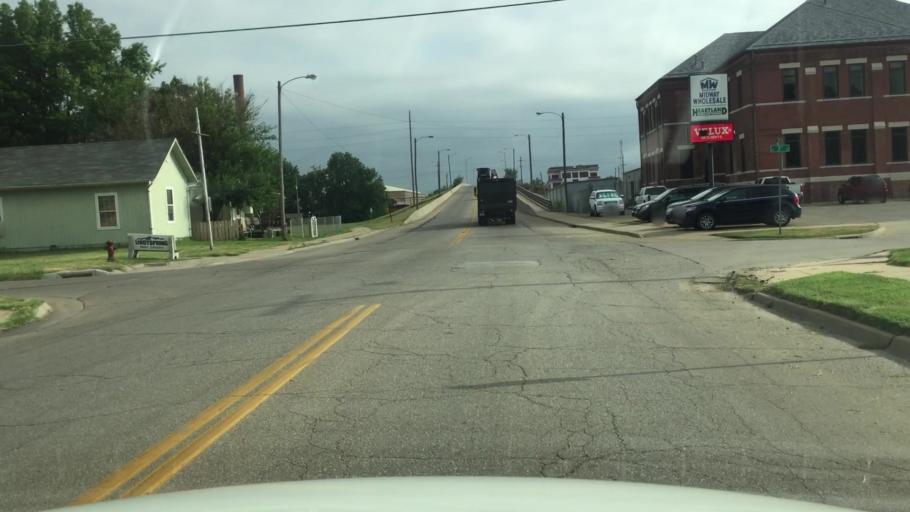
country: US
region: Kansas
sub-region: Shawnee County
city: Topeka
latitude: 39.0526
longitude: -95.6593
